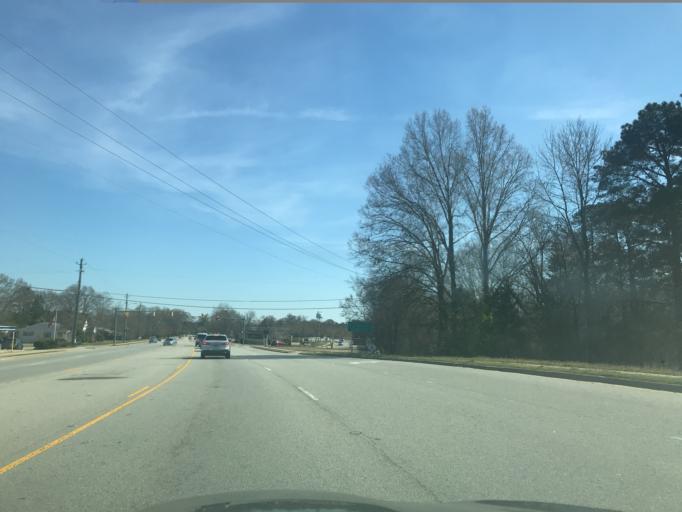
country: US
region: North Carolina
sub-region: Wake County
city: Fuquay-Varina
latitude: 35.6000
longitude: -78.8018
